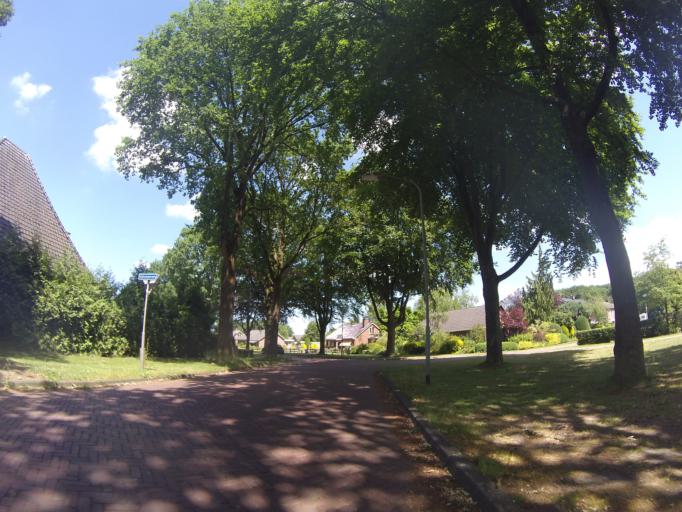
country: NL
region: Drenthe
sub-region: Gemeente Emmen
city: Emmen
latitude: 52.8496
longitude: 6.8533
